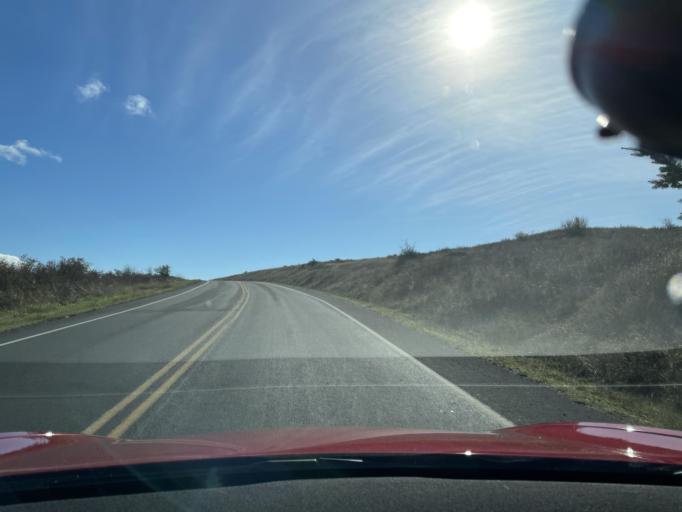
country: US
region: Washington
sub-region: San Juan County
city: Friday Harbor
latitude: 48.4652
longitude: -123.0054
